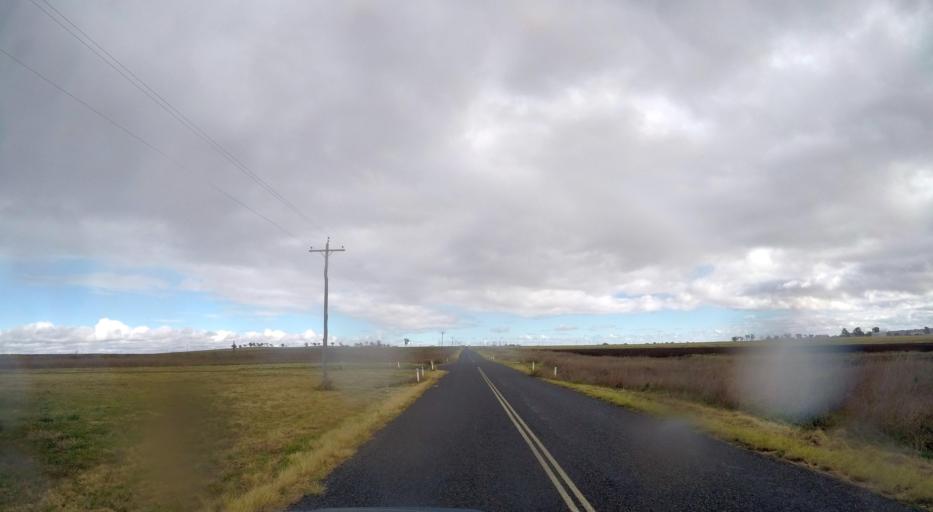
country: AU
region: Queensland
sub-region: Southern Downs
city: Warwick
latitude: -28.0551
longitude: 152.0235
